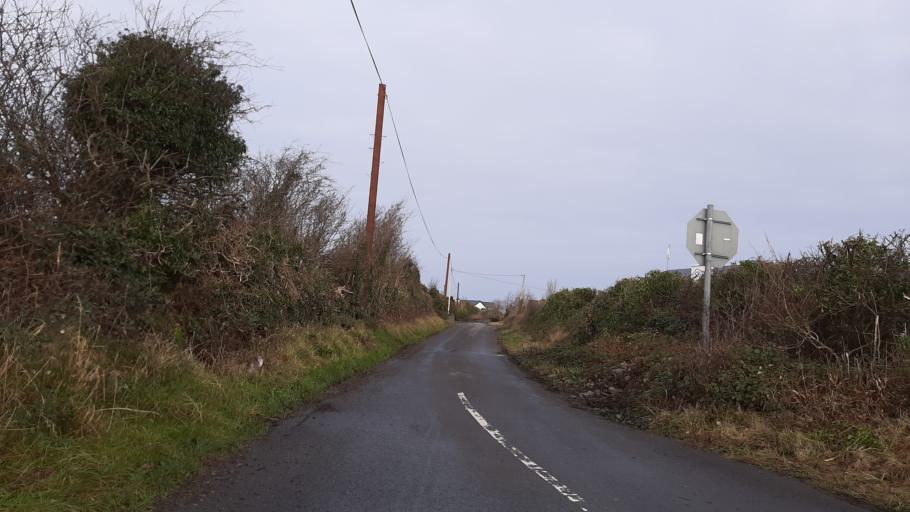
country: IE
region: Connaught
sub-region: County Galway
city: Gaillimh
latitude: 53.3133
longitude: -9.0526
